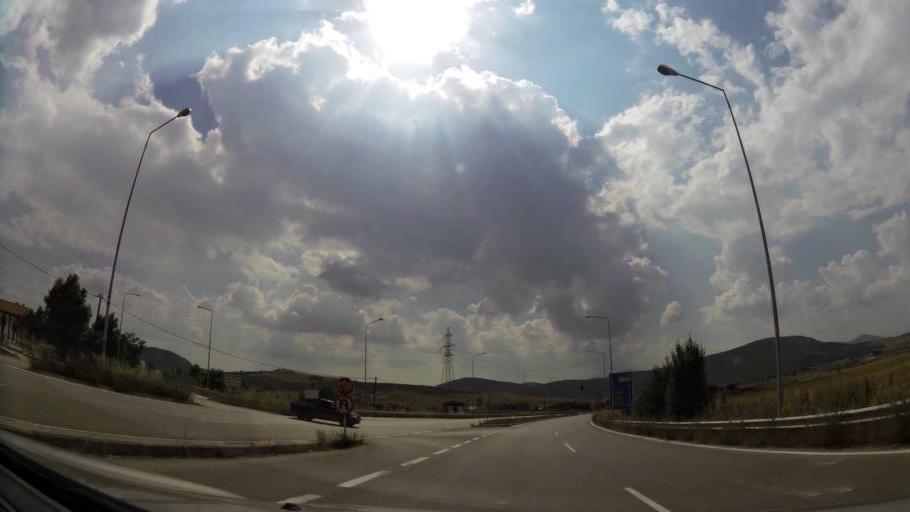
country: GR
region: West Macedonia
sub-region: Nomos Kozanis
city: Koila
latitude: 40.3418
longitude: 21.8130
